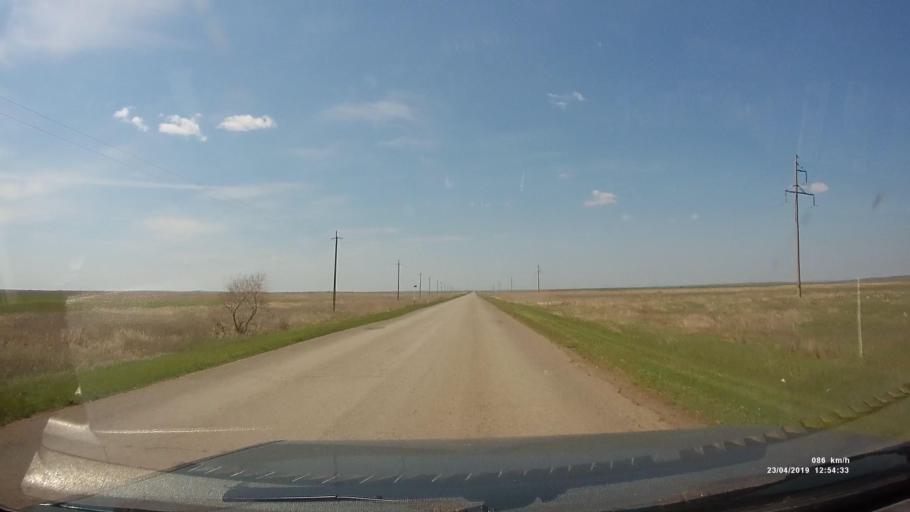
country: RU
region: Kalmykiya
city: Yashalta
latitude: 46.5807
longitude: 42.5766
